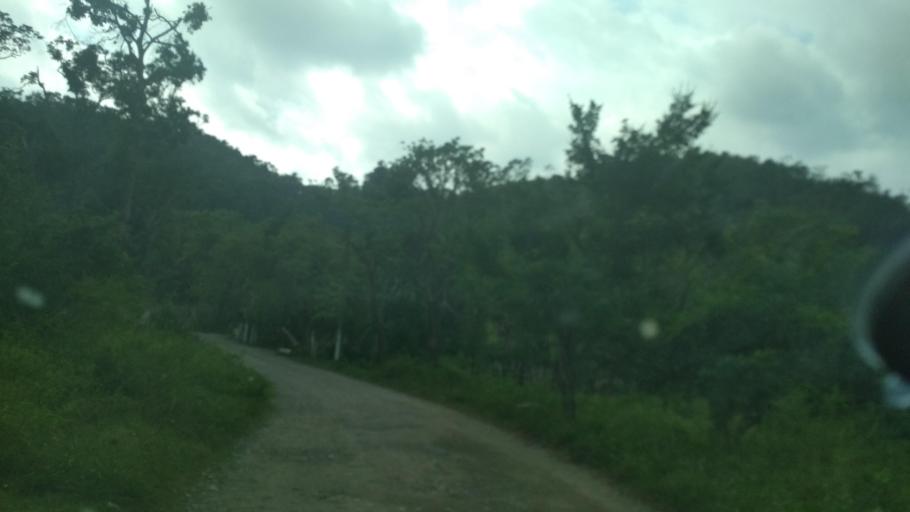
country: MX
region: Veracruz
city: Papantla de Olarte
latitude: 20.4773
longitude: -97.3575
